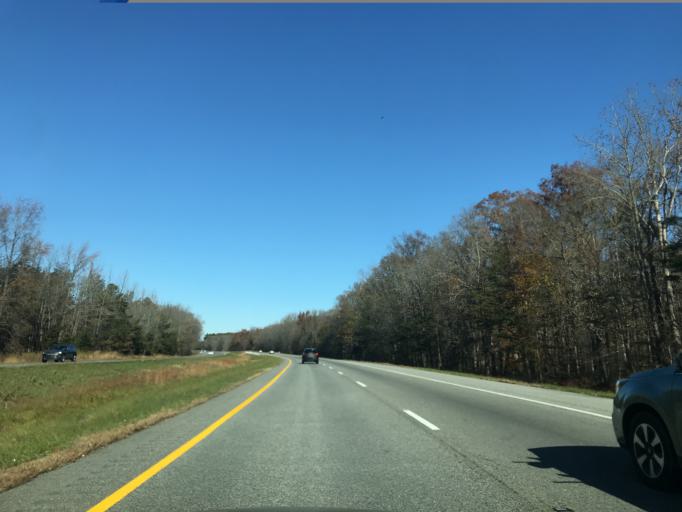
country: US
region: Maryland
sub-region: Queen Anne's County
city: Kingstown
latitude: 39.2278
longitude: -75.8752
